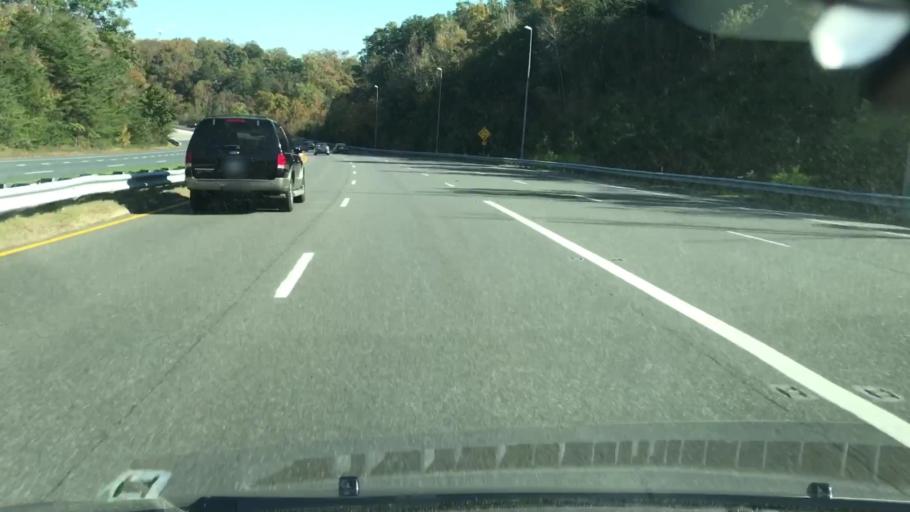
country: US
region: Virginia
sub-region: Fairfax County
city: West Springfield
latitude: 38.7606
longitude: -77.2110
